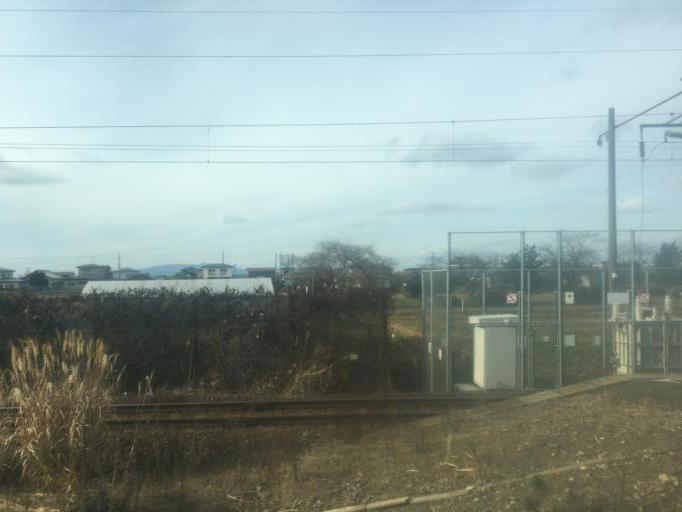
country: JP
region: Akita
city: Tenno
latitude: 39.8980
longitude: 140.0729
